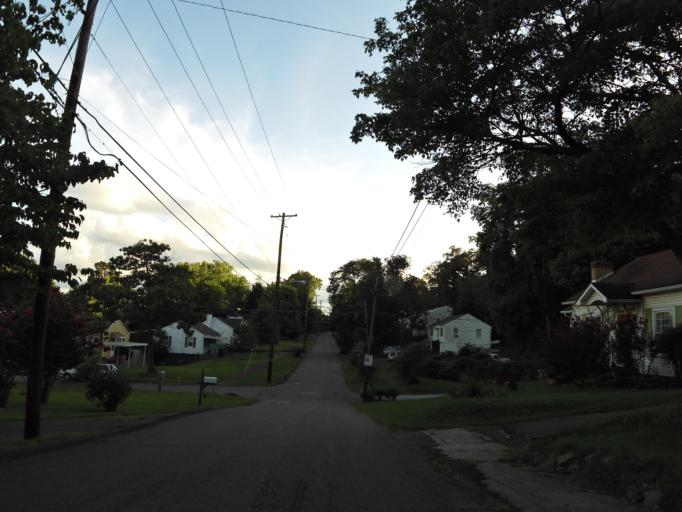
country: US
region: Tennessee
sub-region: Knox County
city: Knoxville
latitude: 36.0075
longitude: -83.9316
